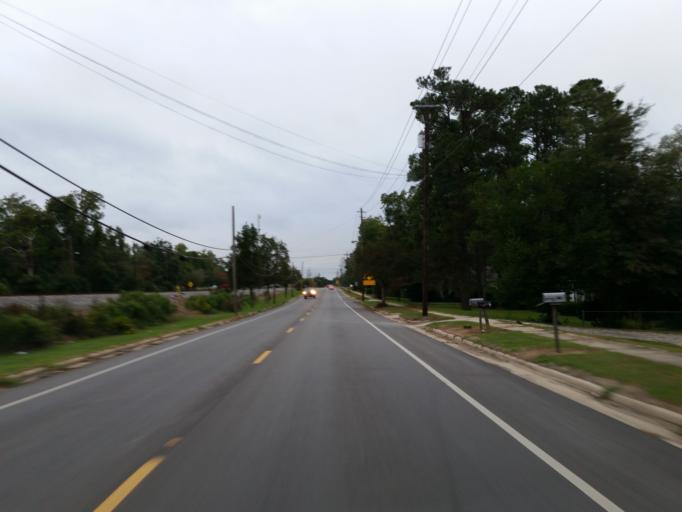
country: US
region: Georgia
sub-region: Turner County
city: Ashburn
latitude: 31.6988
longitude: -83.6499
